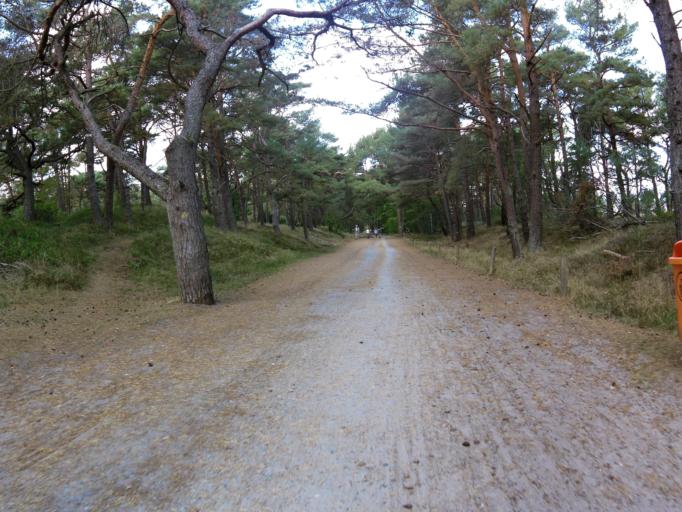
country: DE
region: Mecklenburg-Vorpommern
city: Ostseebad Zinnowitz
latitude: 54.0916
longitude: 13.8889
